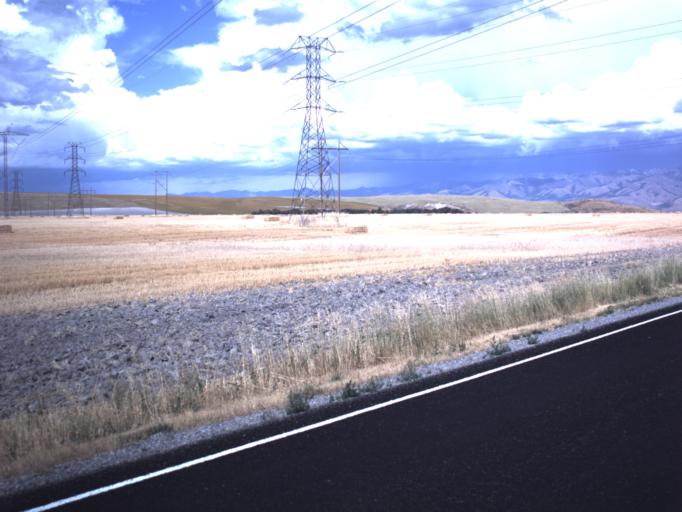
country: US
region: Utah
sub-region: Cache County
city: Benson
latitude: 41.9175
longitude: -112.0015
